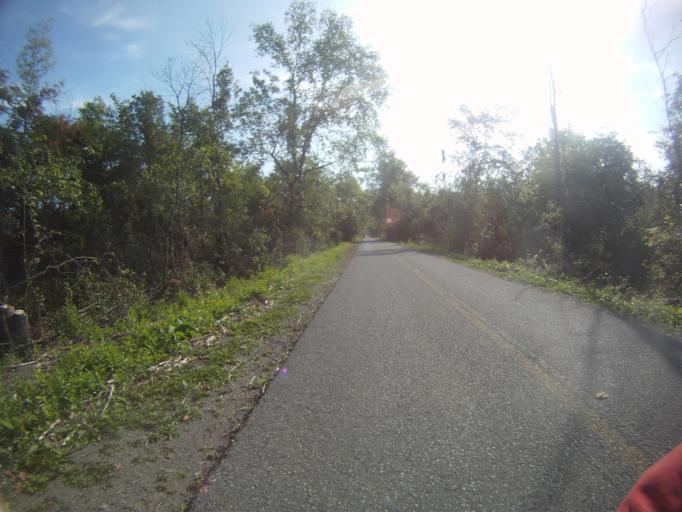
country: CA
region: Ontario
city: Bells Corners
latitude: 45.3412
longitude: -75.8604
